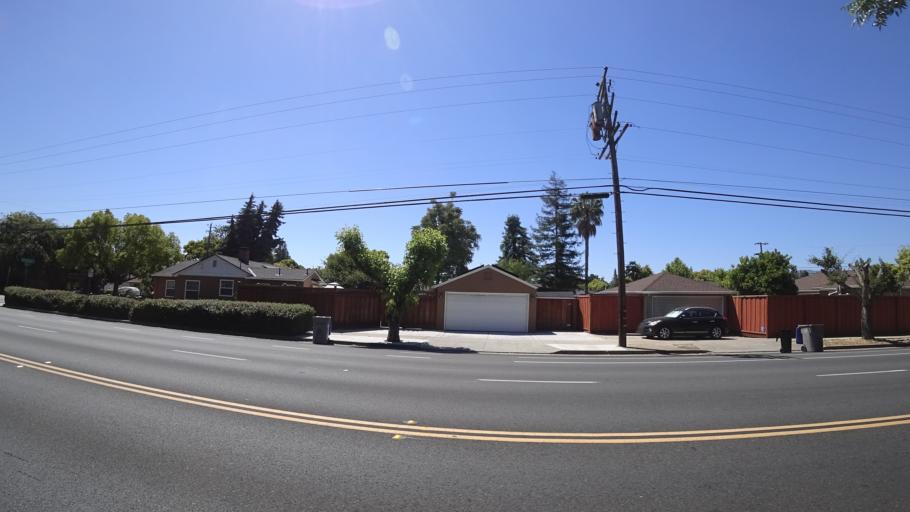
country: US
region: California
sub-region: Santa Clara County
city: Buena Vista
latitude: 37.2866
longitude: -121.8961
